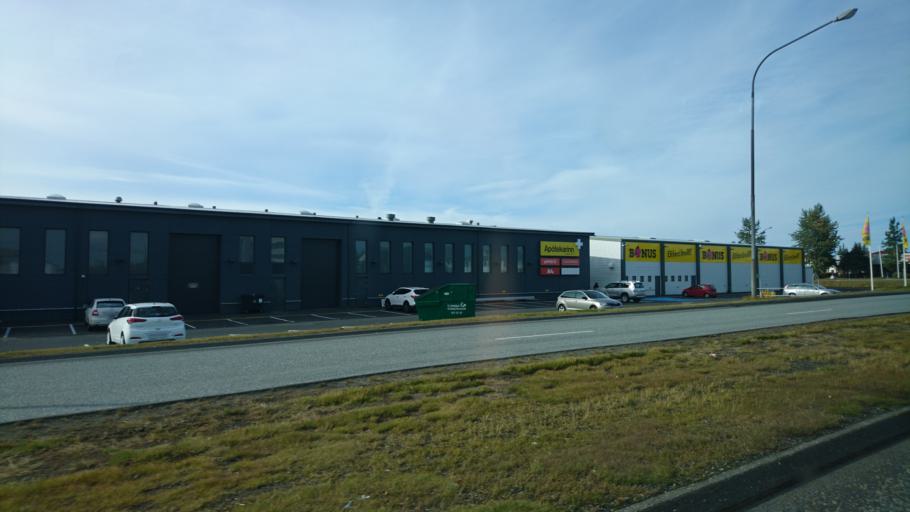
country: IS
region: Capital Region
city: Hafnarfjoerdur
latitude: 64.0771
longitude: -21.9406
